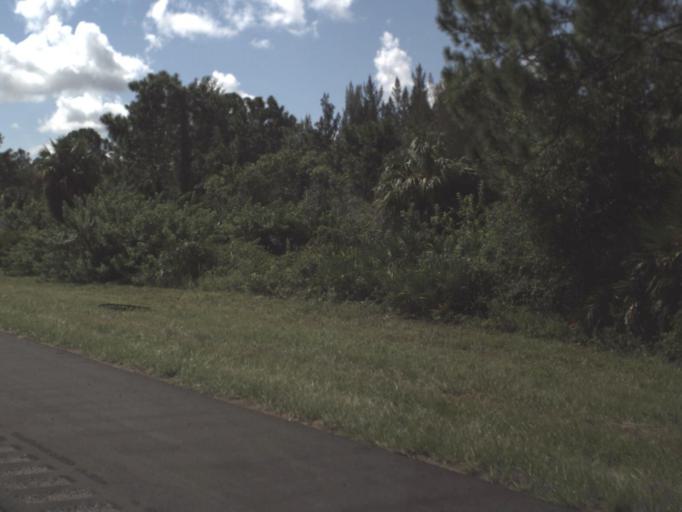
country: US
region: Florida
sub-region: Lee County
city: Suncoast Estates
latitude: 26.7371
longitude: -81.8479
